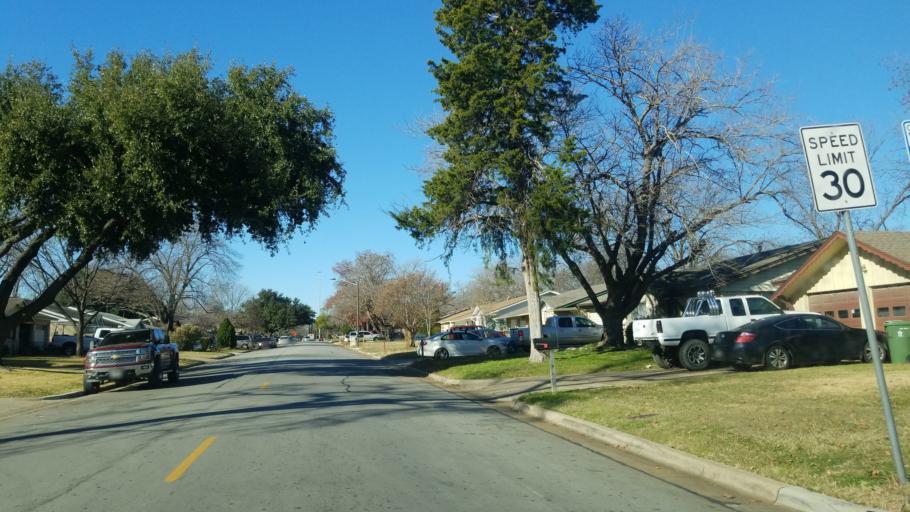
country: US
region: Texas
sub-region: Tarrant County
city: Arlington
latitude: 32.7260
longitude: -97.0580
